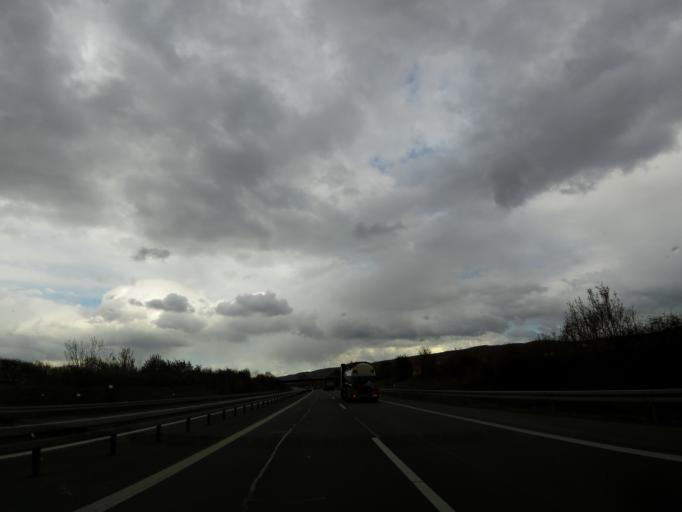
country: DE
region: Saxony-Anhalt
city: Wernigerode
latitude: 51.8555
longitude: 10.8071
